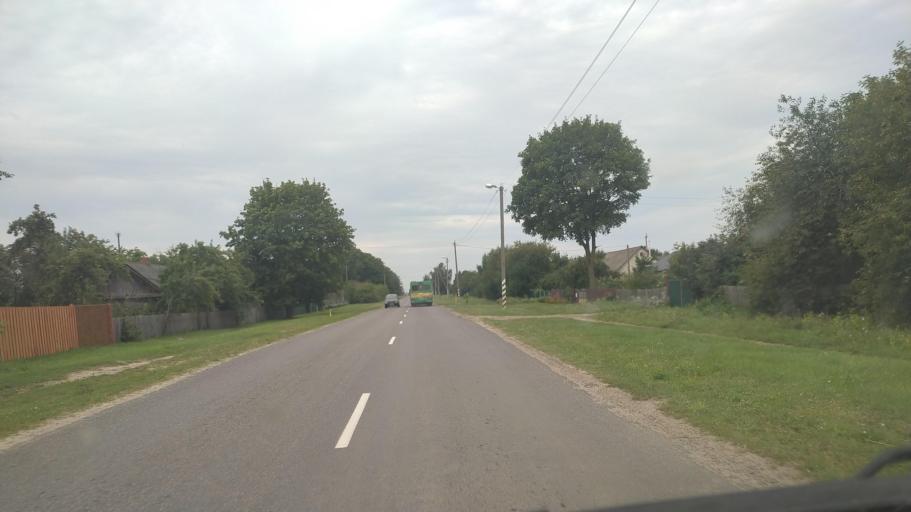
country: BY
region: Brest
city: Byaroza
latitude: 52.5817
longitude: 24.8604
